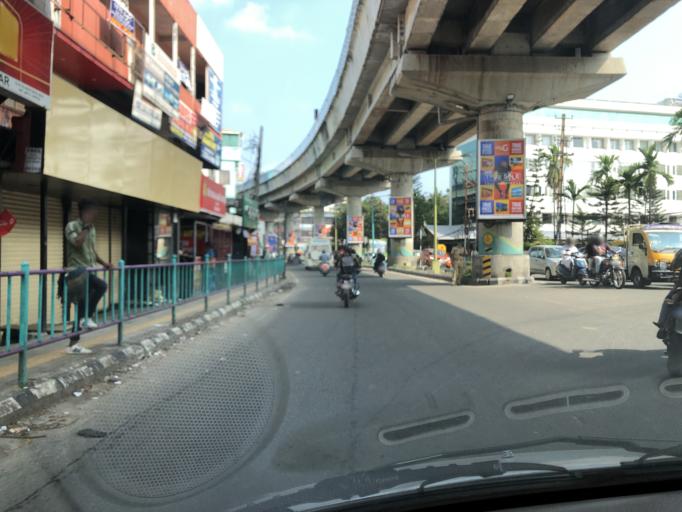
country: IN
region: Kerala
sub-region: Ernakulam
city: Elur
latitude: 10.0045
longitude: 76.3050
